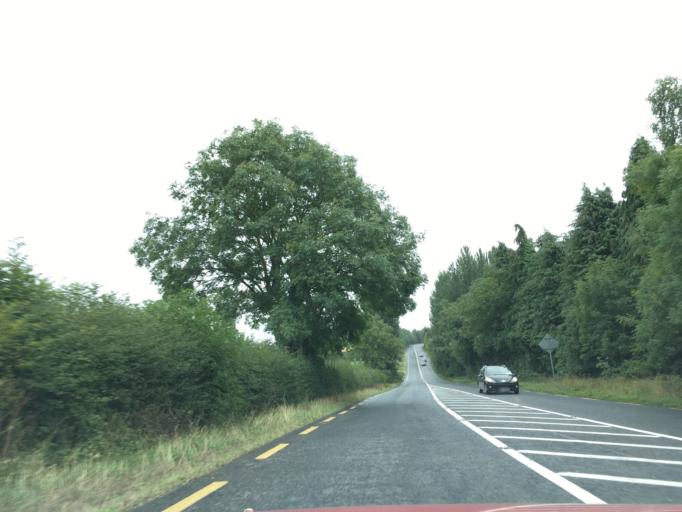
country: IE
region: Munster
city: Carrick-on-Suir
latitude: 52.3654
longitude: -7.5139
